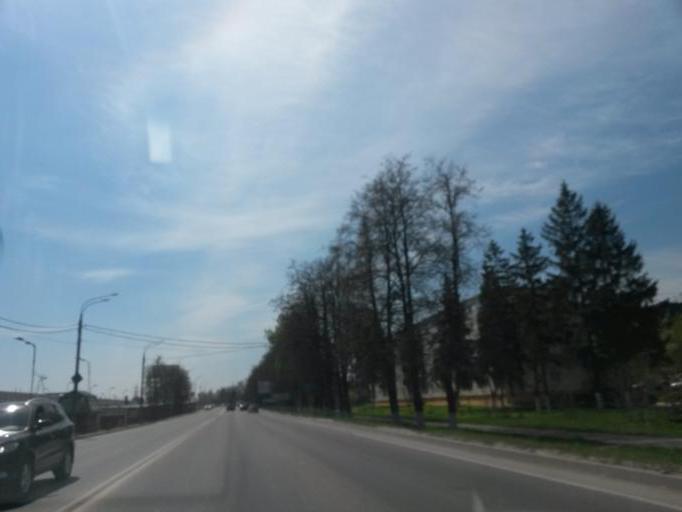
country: RU
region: Moskovskaya
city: Klimovsk
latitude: 55.3889
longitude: 37.5409
